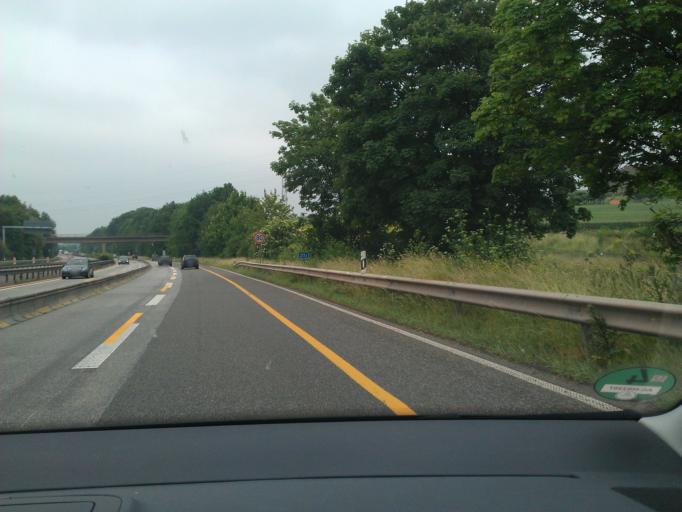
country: DE
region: Rheinland-Pfalz
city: Plaidt
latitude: 50.3778
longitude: 7.3906
